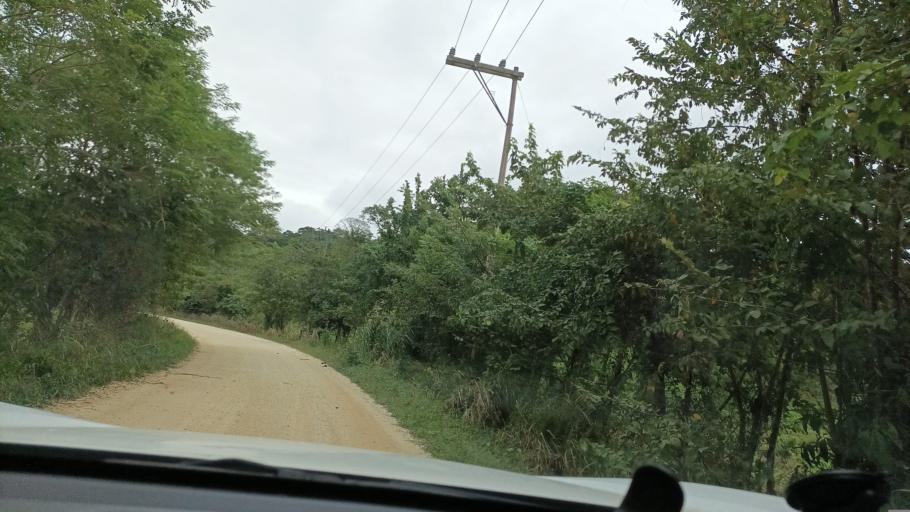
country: MX
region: Veracruz
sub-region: Moloacan
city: Cuichapa
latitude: 17.8331
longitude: -94.3524
